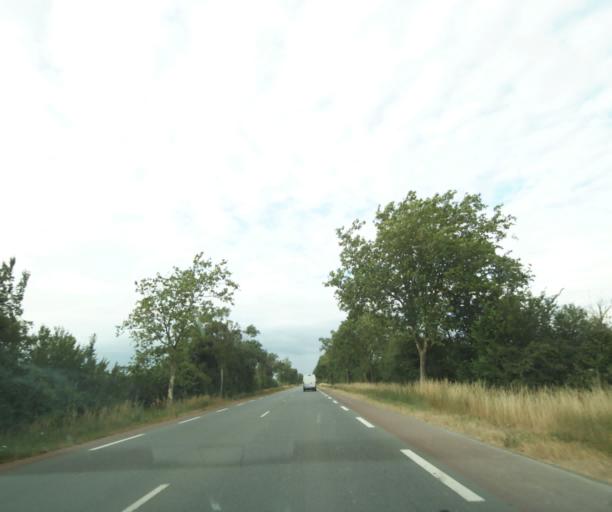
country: FR
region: Poitou-Charentes
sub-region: Departement de la Charente-Maritime
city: Marans
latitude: 46.2796
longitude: -0.9972
